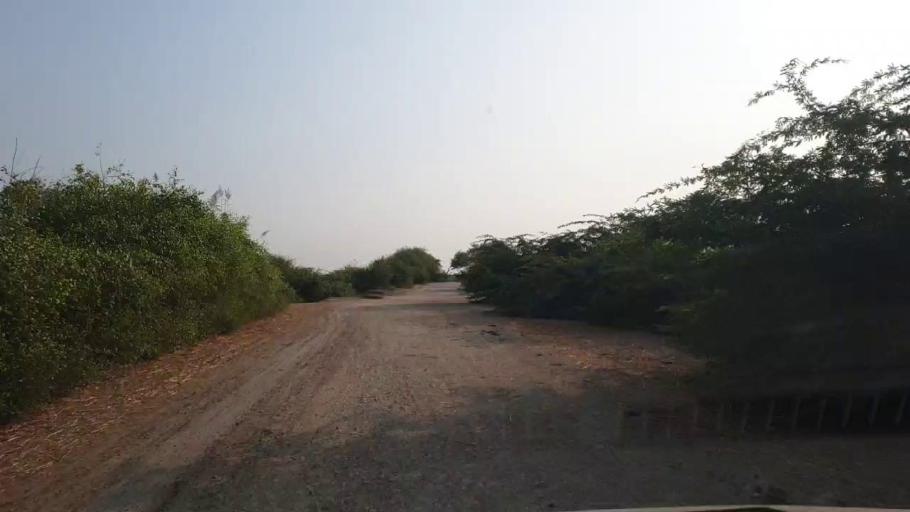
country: PK
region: Sindh
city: Rajo Khanani
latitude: 25.0129
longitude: 68.7871
